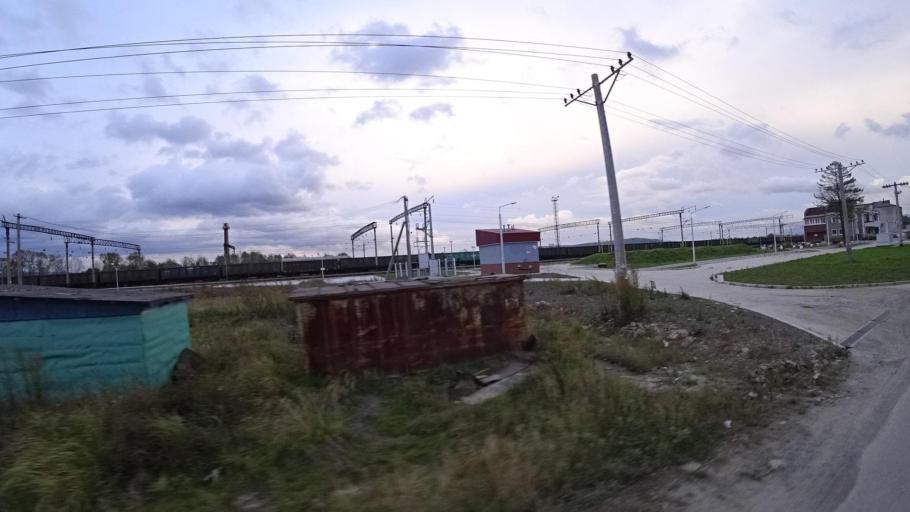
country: RU
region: Jewish Autonomous Oblast
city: Izvestkovyy
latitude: 48.9837
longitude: 131.5544
